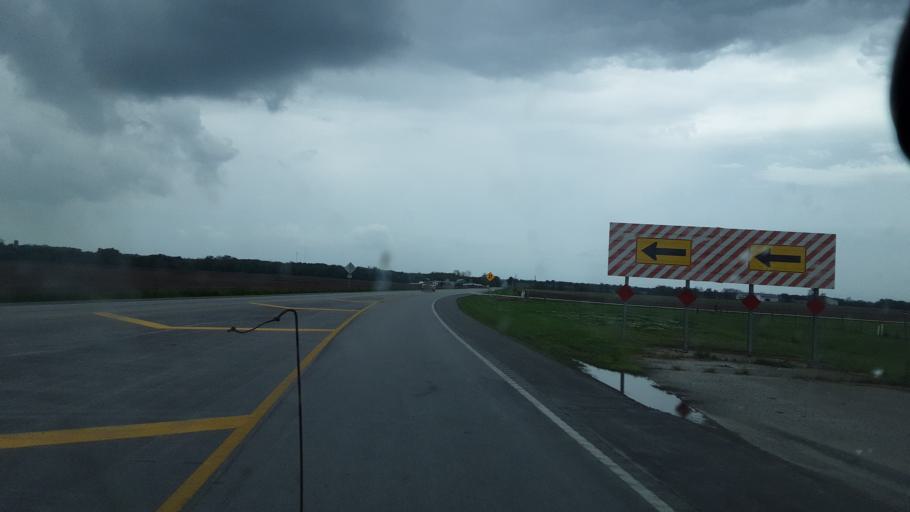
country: US
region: Missouri
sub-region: Marion County
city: Palmyra
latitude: 39.7355
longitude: -91.5101
